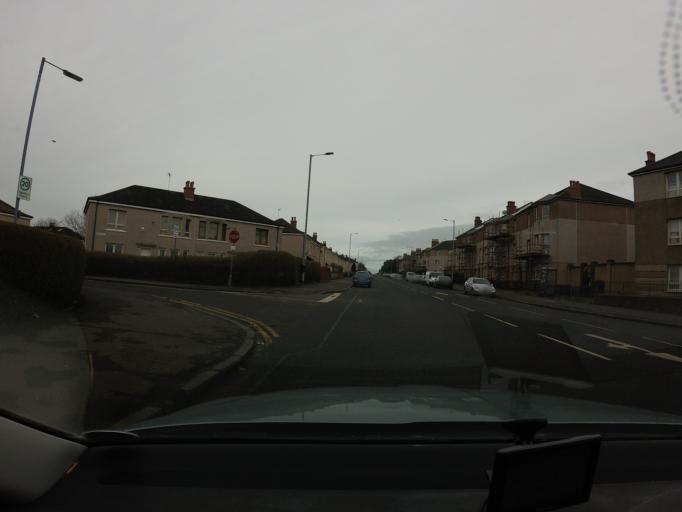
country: GB
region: Scotland
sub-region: Glasgow City
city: Glasgow
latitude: 55.8356
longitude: -4.2492
